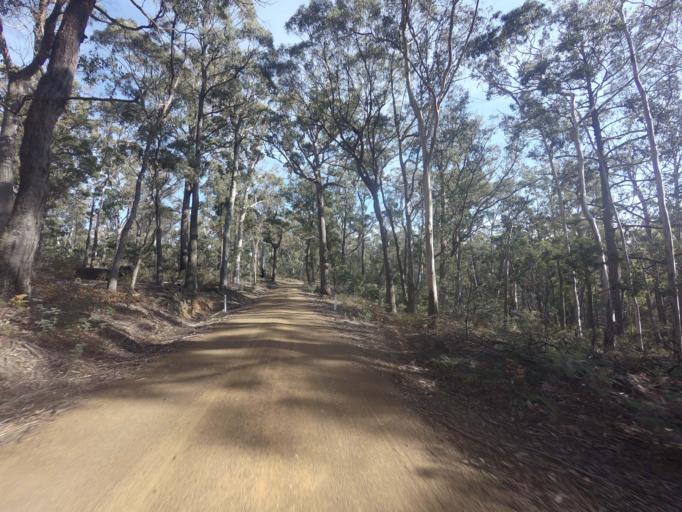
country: AU
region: Tasmania
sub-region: Sorell
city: Sorell
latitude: -42.5238
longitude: 147.4717
